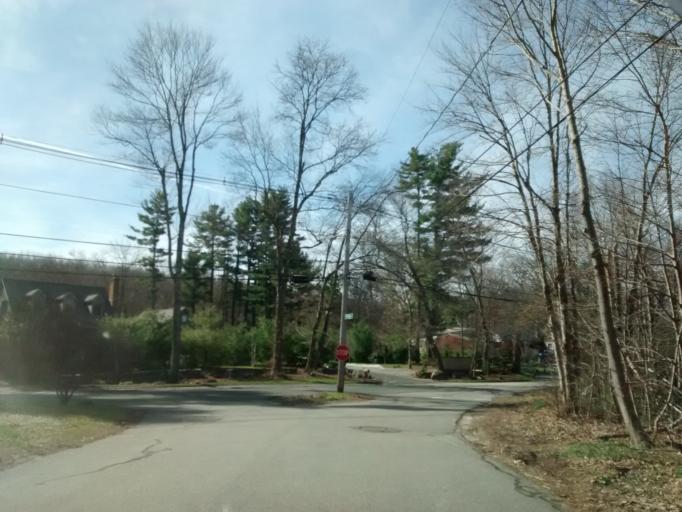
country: US
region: Massachusetts
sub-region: Worcester County
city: Millbury
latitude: 42.2040
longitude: -71.7481
